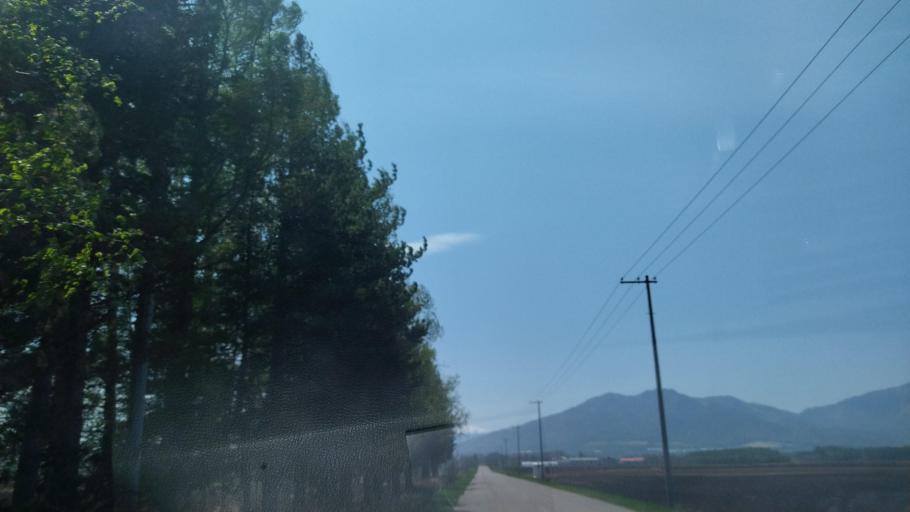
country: JP
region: Hokkaido
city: Obihiro
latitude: 42.9042
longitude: 142.9865
